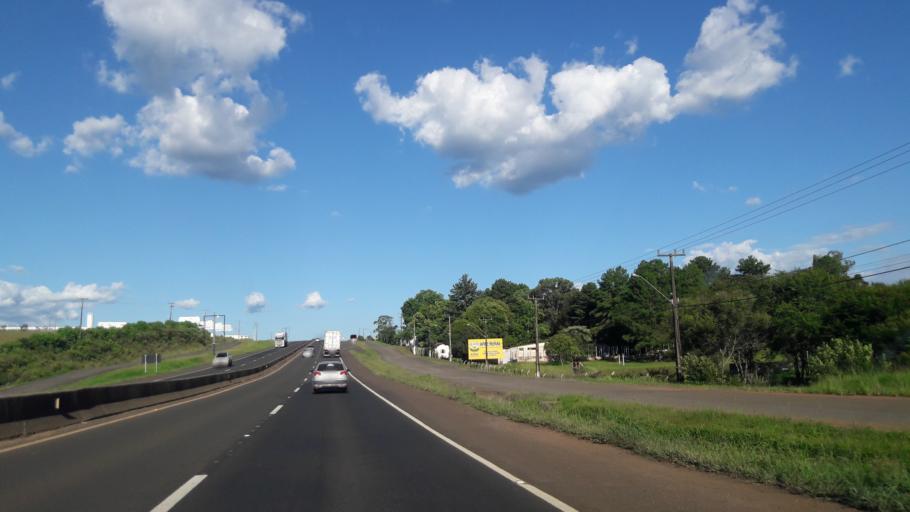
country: BR
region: Parana
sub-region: Guarapuava
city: Guarapuava
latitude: -25.3476
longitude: -51.4520
